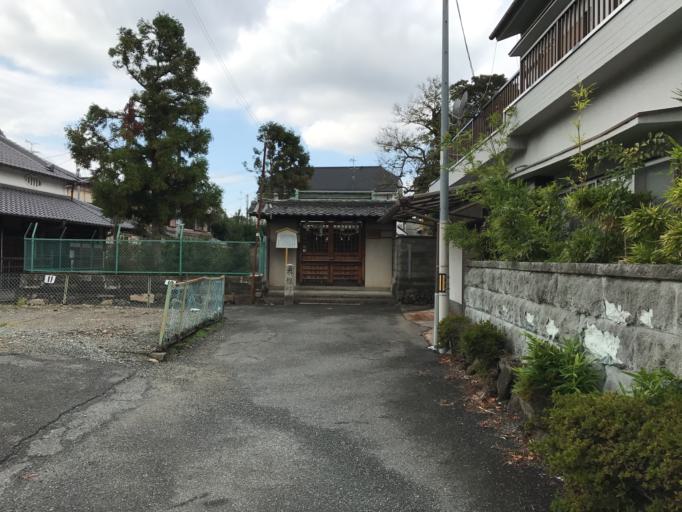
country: JP
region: Osaka
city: Kashihara
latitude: 34.5670
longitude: 135.6168
